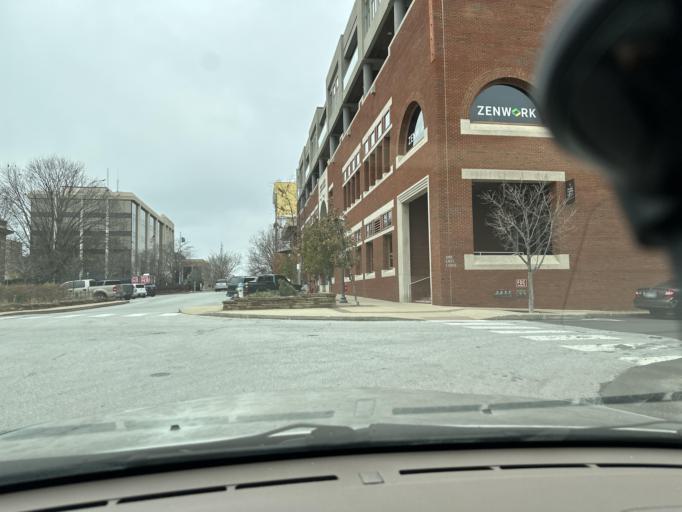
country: US
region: Arkansas
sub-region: Washington County
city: Fayetteville
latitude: 36.0618
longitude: -94.1597
